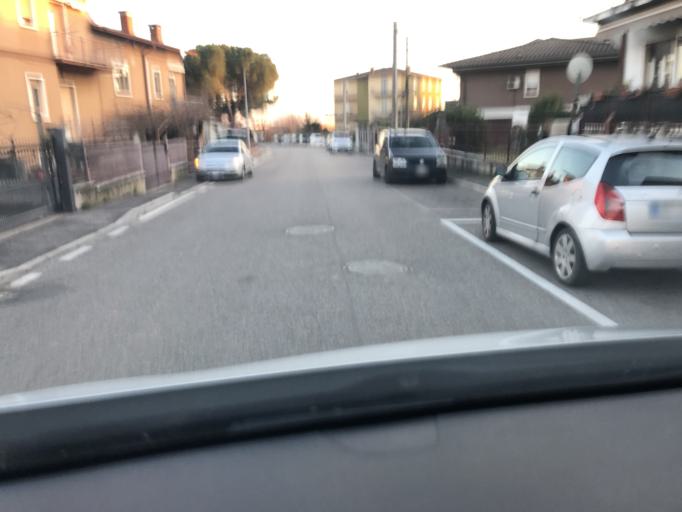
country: IT
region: Veneto
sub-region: Provincia di Verona
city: Sommacampagna
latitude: 45.3990
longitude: 10.8432
